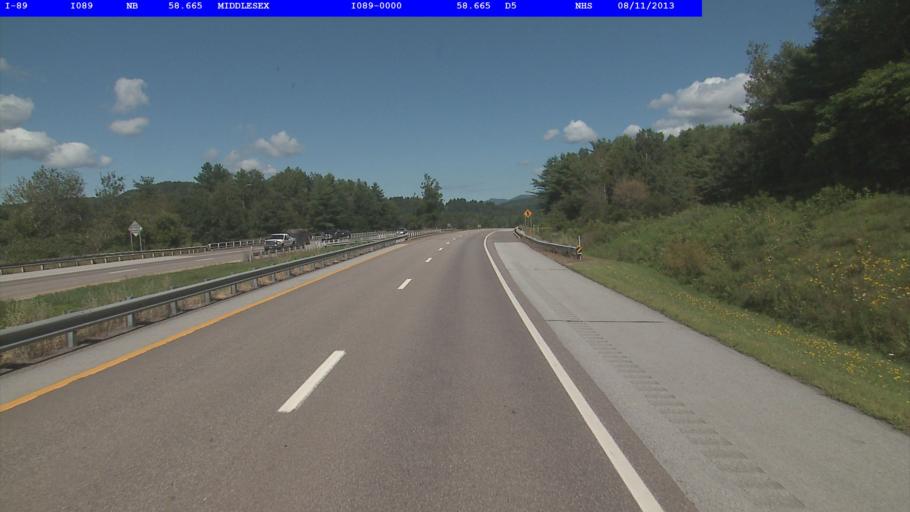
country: US
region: Vermont
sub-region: Washington County
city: Waterbury
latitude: 44.2976
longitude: -72.6843
